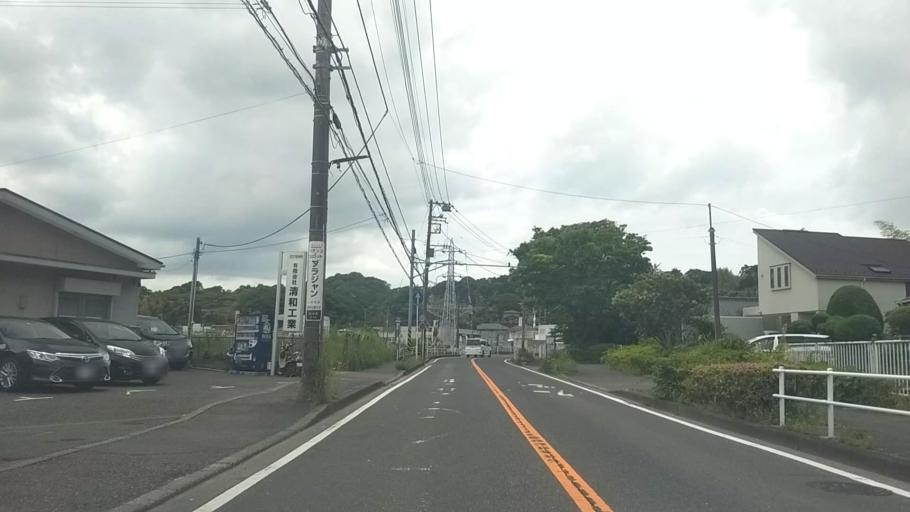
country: JP
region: Kanagawa
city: Fujisawa
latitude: 35.3664
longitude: 139.5225
